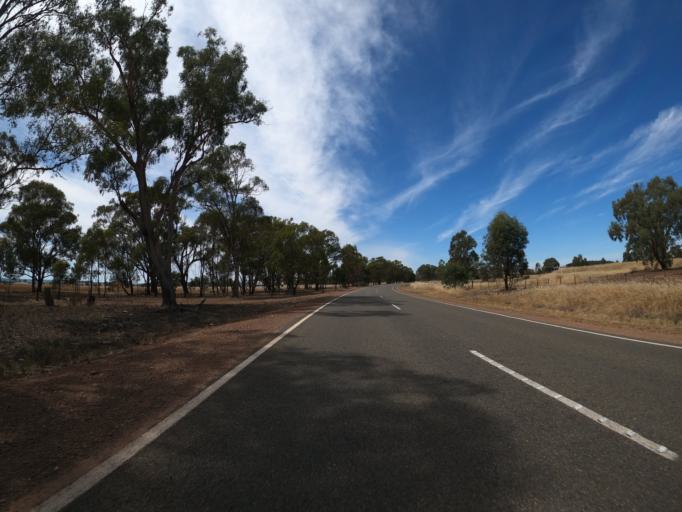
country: AU
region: Victoria
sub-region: Benalla
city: Benalla
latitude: -36.3062
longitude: 145.9578
